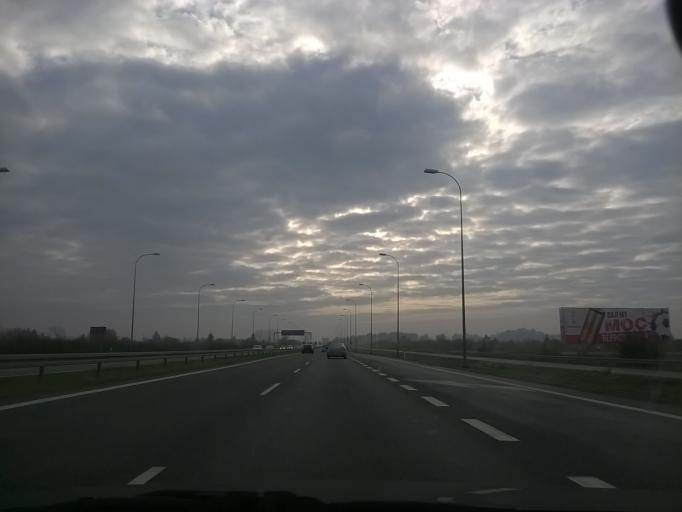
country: PL
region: Pomeranian Voivodeship
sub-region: Powiat nowodworski
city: Nowy Dwor Gdanski
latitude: 54.2095
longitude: 19.1058
